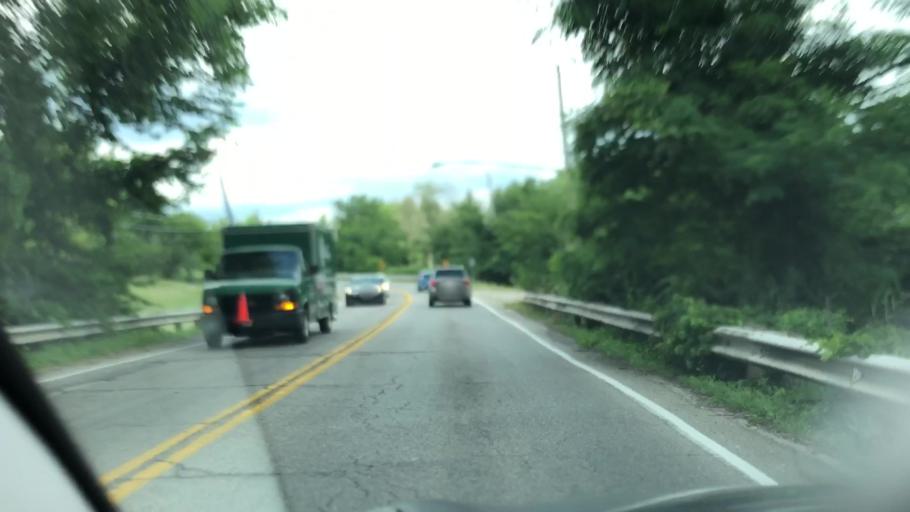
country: US
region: Ohio
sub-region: Summit County
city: Fairlawn
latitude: 41.1272
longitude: -81.6344
